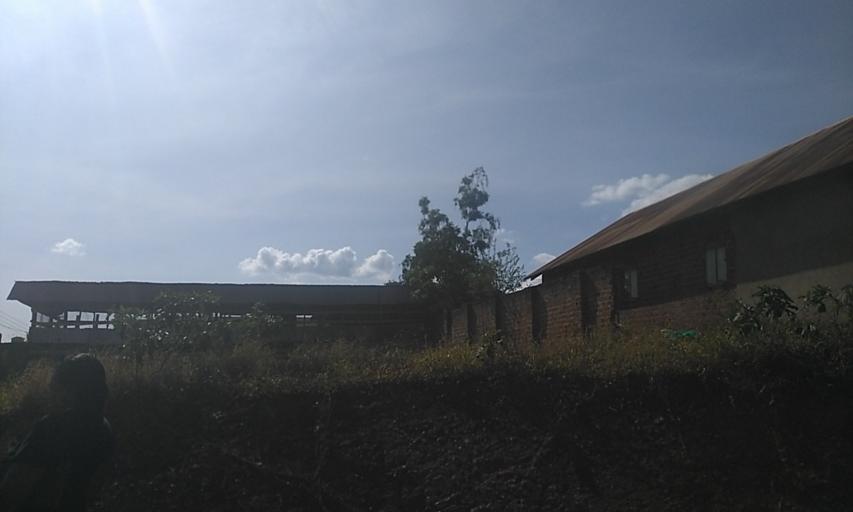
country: UG
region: Central Region
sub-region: Wakiso District
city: Kireka
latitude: 0.3803
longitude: 32.6258
